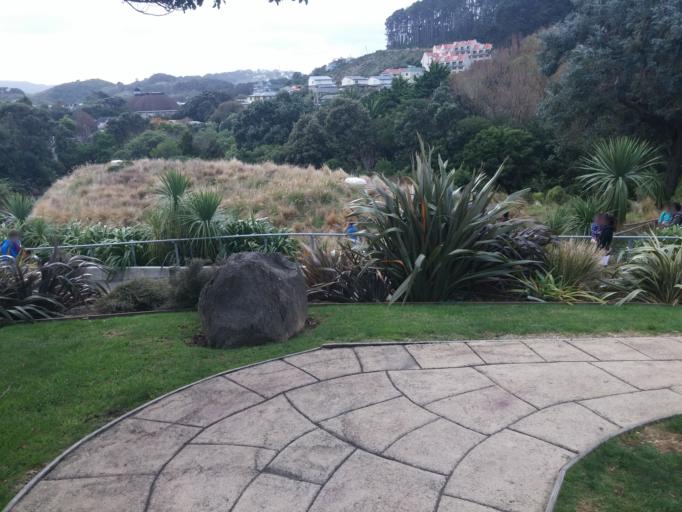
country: NZ
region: Wellington
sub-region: Wellington City
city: Brooklyn
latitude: -41.3207
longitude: 174.7843
